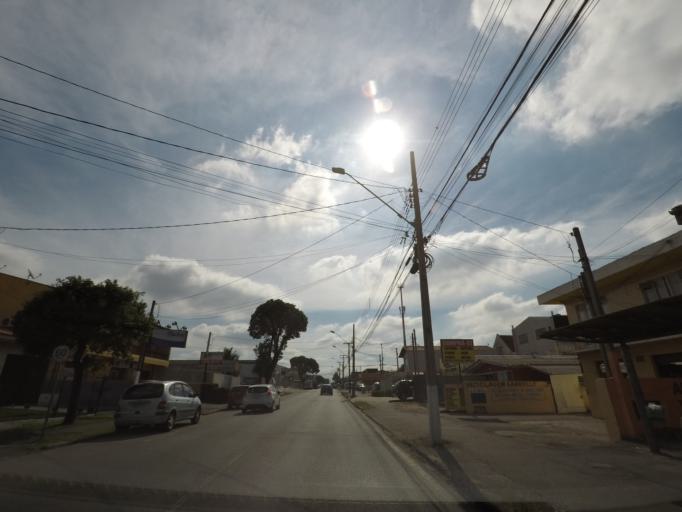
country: BR
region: Parana
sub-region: Sao Jose Dos Pinhais
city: Sao Jose dos Pinhais
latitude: -25.5095
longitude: -49.2781
